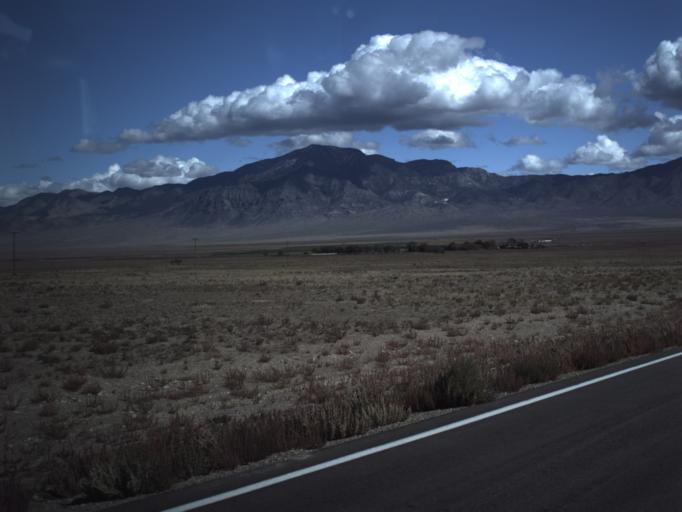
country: US
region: Utah
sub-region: Beaver County
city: Milford
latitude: 38.4840
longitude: -113.4486
